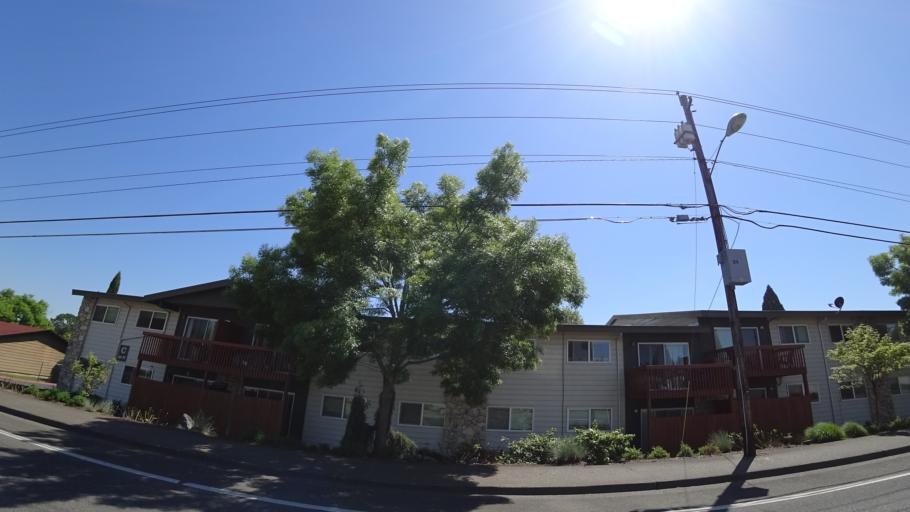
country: US
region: Oregon
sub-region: Washington County
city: Beaverton
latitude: 45.4938
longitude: -122.8010
